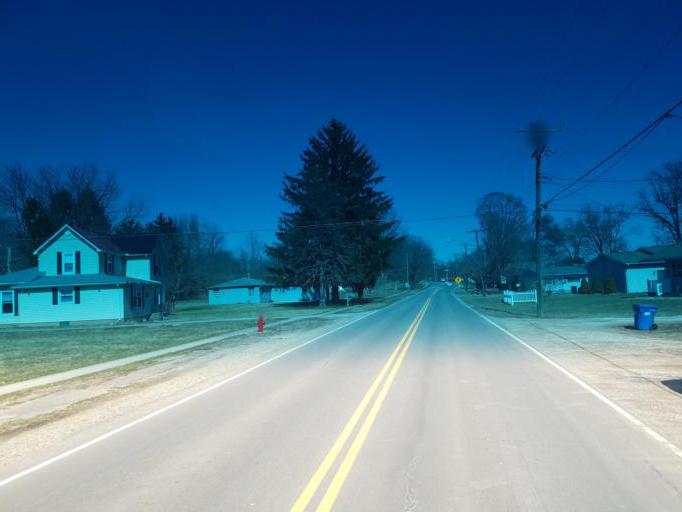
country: US
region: Ohio
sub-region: Knox County
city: Mount Vernon
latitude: 40.4026
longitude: -82.4704
